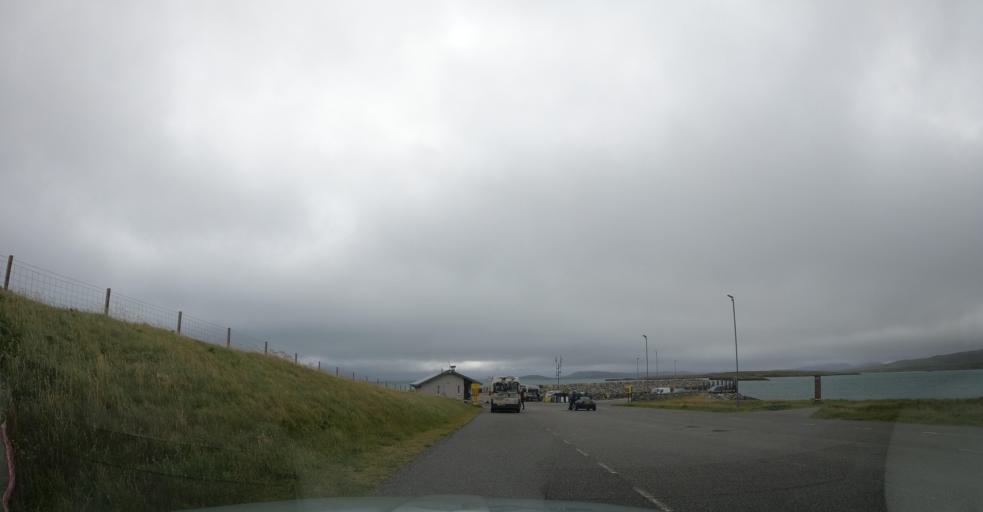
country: GB
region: Scotland
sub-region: Eilean Siar
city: Isle of North Uist
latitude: 57.7034
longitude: -7.1810
